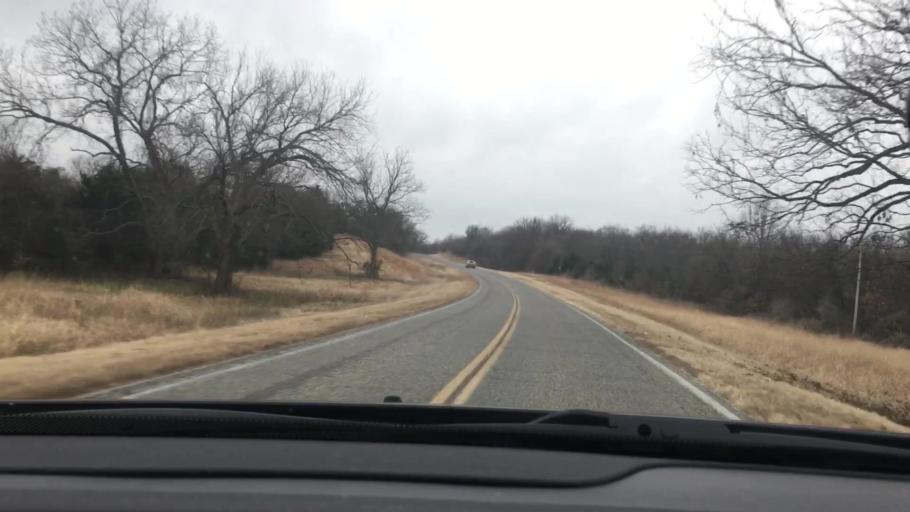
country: US
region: Oklahoma
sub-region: Johnston County
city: Tishomingo
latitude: 34.2259
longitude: -96.6358
